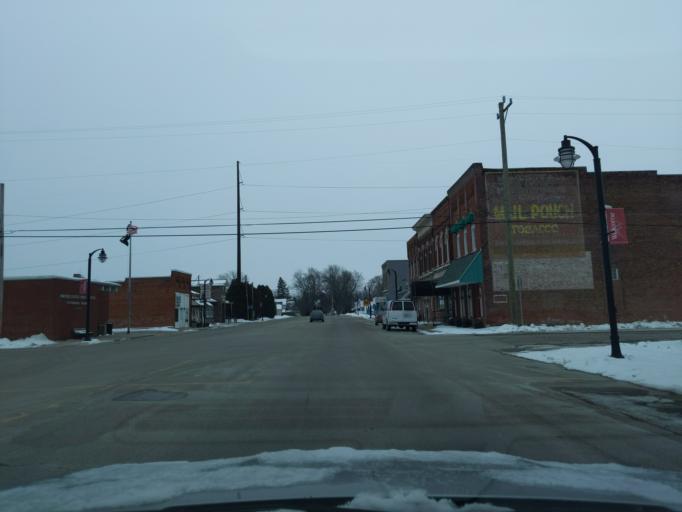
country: US
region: Indiana
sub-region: Benton County
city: Otterbein
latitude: 40.4899
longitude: -87.0963
